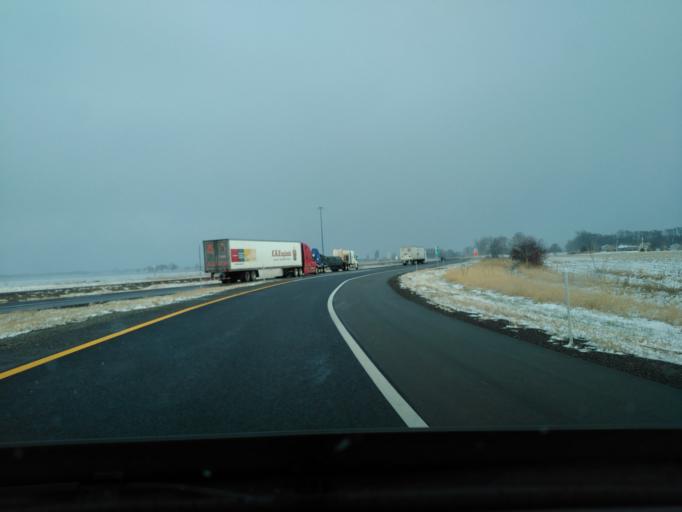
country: US
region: Illinois
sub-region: Madison County
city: Highland
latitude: 38.7859
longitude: -89.6287
